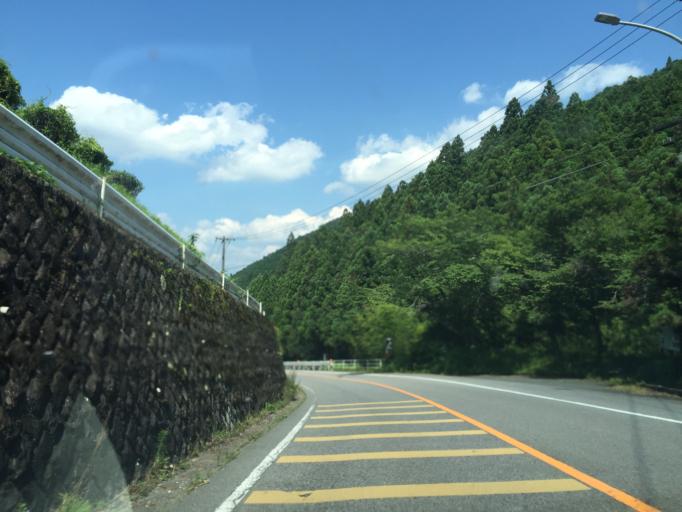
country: JP
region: Aichi
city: Shinshiro
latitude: 35.0219
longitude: 137.6989
